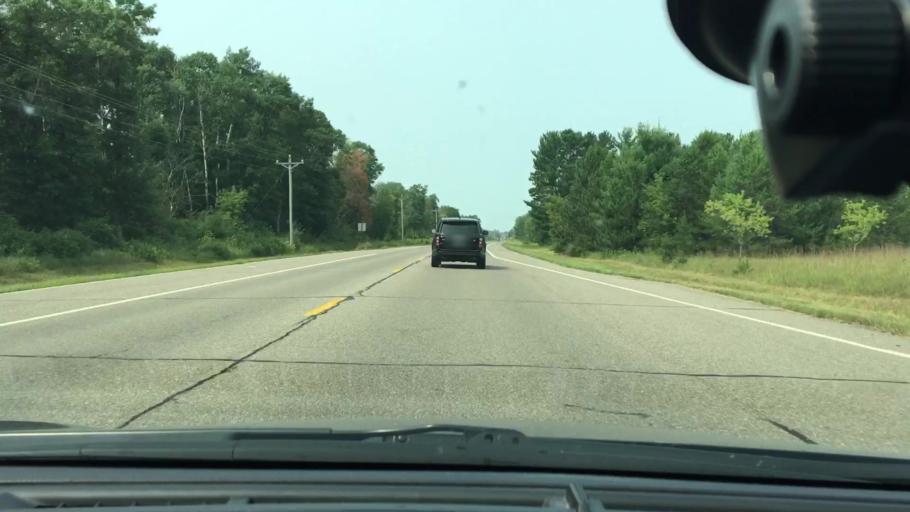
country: US
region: Minnesota
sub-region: Crow Wing County
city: Brainerd
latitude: 46.3984
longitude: -94.2053
